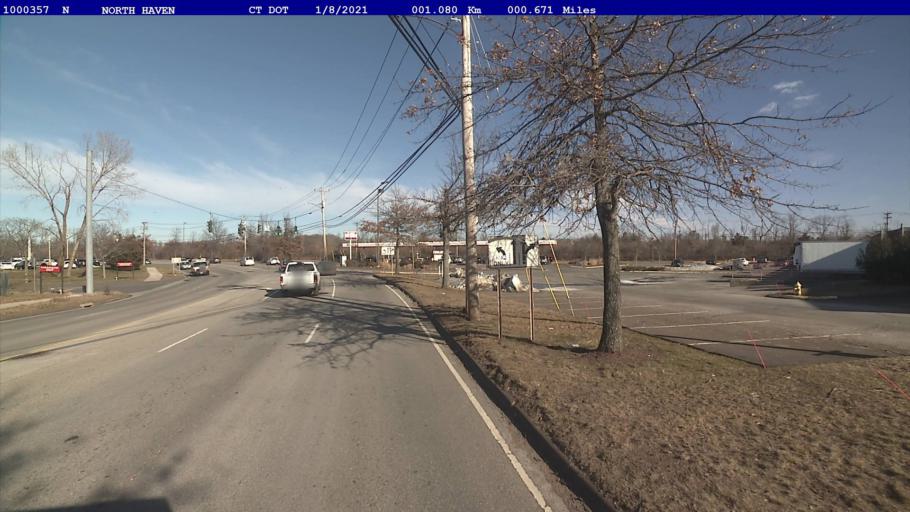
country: US
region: Connecticut
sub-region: New Haven County
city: North Haven
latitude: 41.3595
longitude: -72.8709
